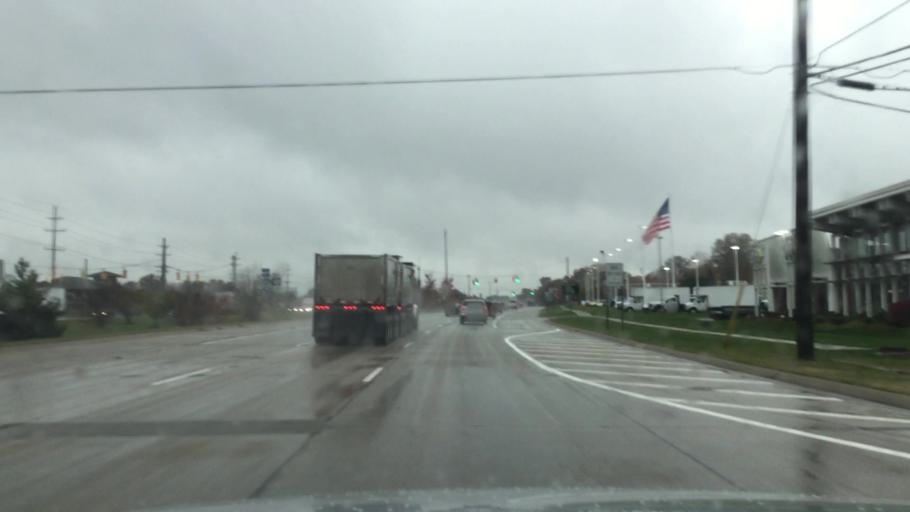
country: US
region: Michigan
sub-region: Macomb County
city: Mount Clemens
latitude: 42.6303
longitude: -82.8561
